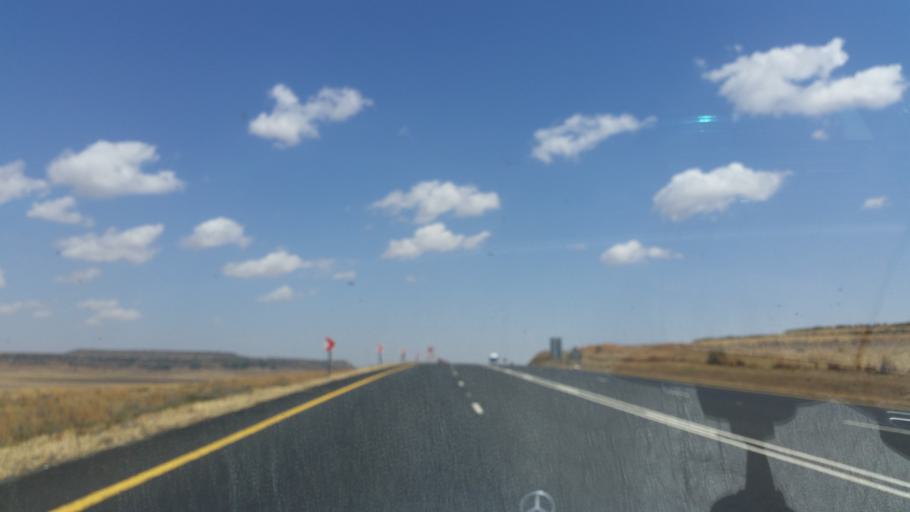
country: ZA
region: Orange Free State
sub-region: Thabo Mofutsanyana District Municipality
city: Senekal
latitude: -28.3095
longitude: 27.8342
